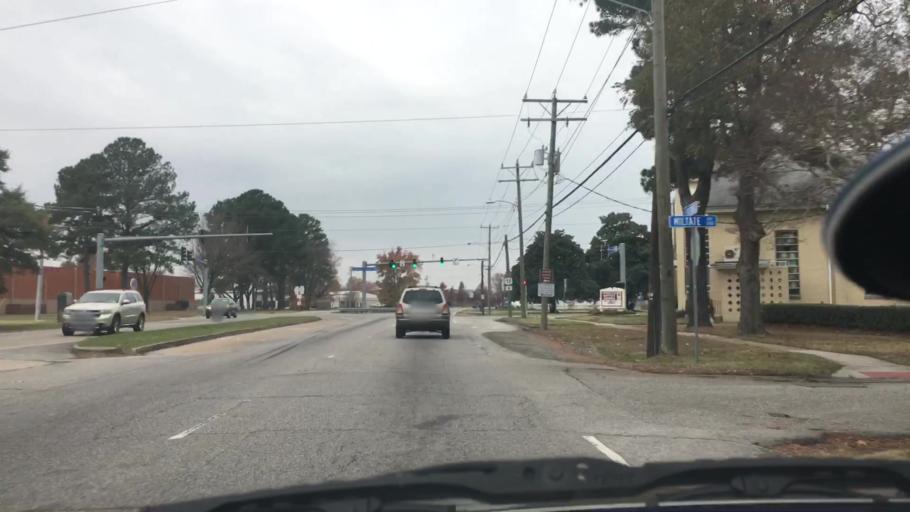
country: US
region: Virginia
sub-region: City of Norfolk
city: Norfolk
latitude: 36.8683
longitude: -76.2288
